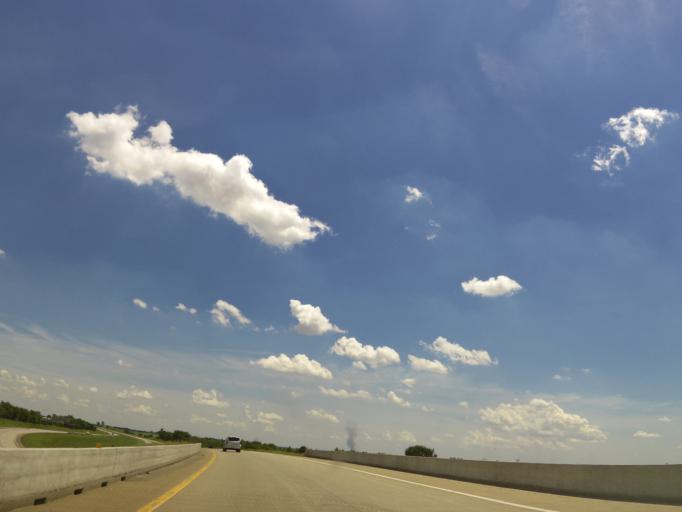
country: US
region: Missouri
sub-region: Pemiscot County
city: Hayti
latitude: 36.2154
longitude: -89.7466
